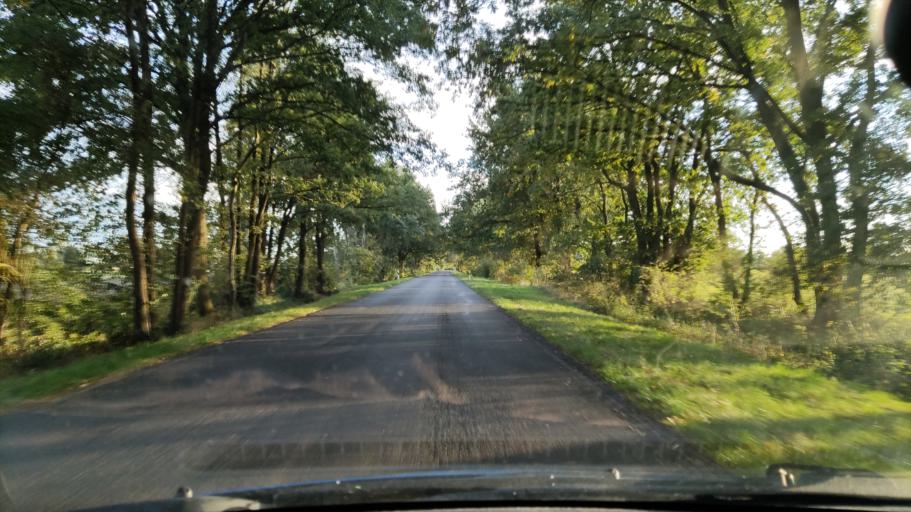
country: DE
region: Lower Saxony
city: Neu Darchau
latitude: 53.3565
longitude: 10.8646
